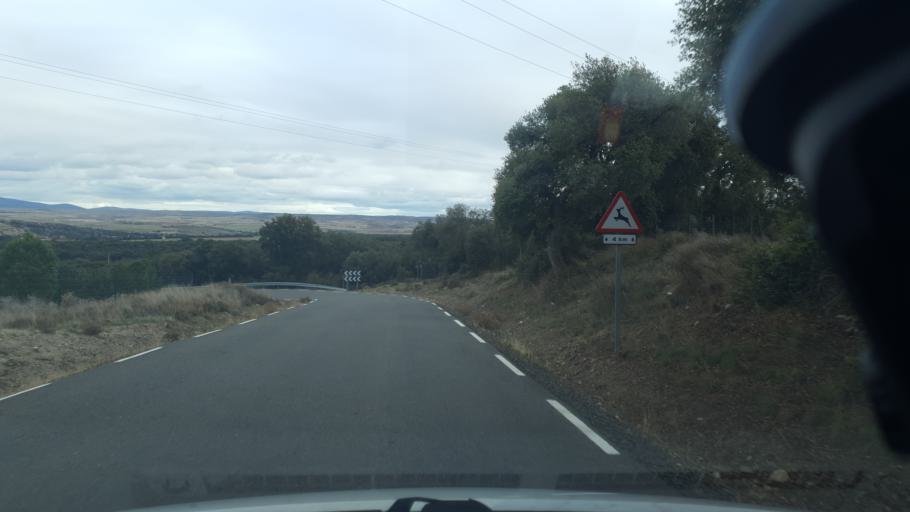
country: ES
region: Castille and Leon
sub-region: Provincia de Avila
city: Gotarrendura
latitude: 40.8255
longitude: -4.7098
